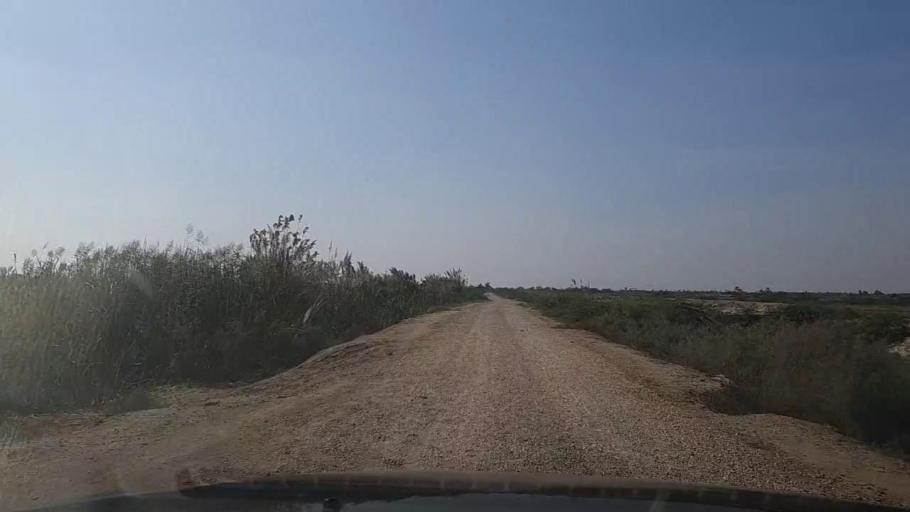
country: PK
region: Sindh
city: Gharo
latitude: 24.7113
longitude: 67.7532
